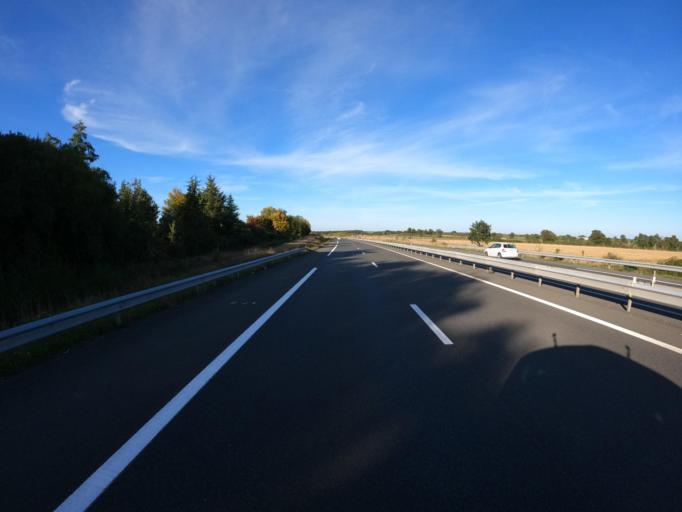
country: FR
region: Pays de la Loire
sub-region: Departement de Maine-et-Loire
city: Saint-Lambert-du-Lattay
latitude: 47.2598
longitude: -0.6166
